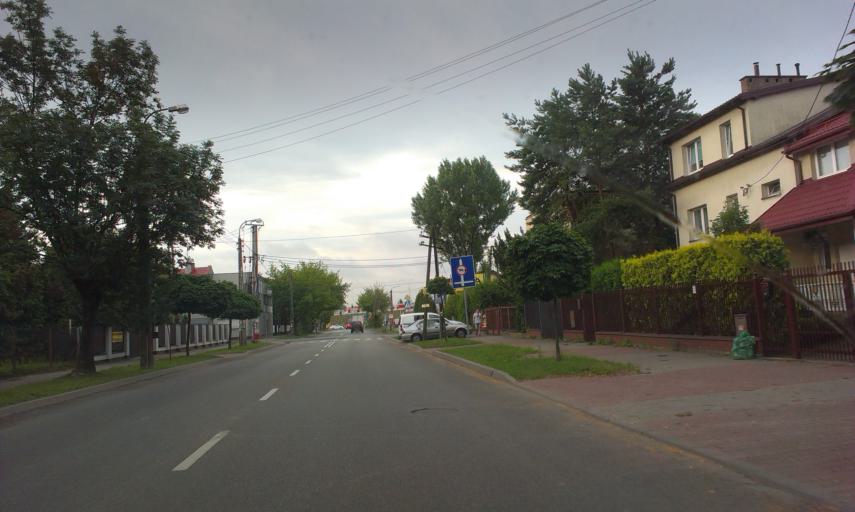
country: PL
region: Masovian Voivodeship
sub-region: Powiat pruszkowski
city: Michalowice
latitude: 52.1833
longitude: 20.8855
